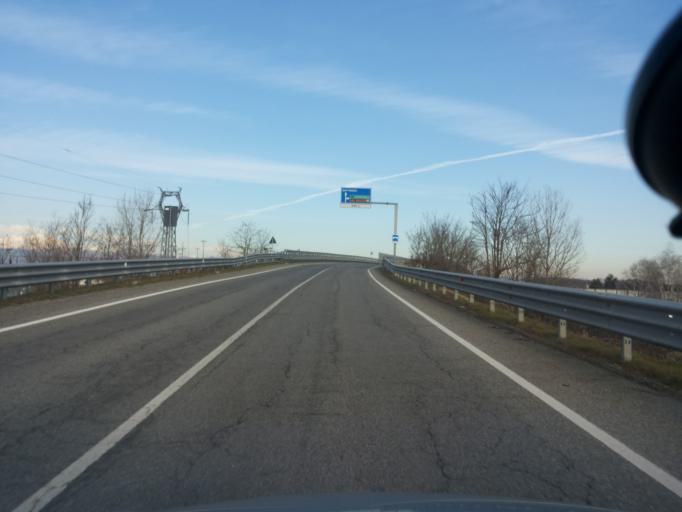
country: IT
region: Piedmont
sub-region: Provincia di Vercelli
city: Greggio
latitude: 45.4597
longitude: 8.3854
